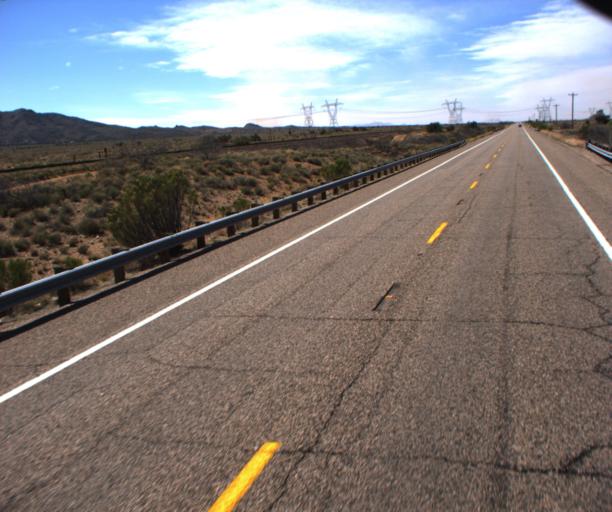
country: US
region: Arizona
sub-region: Mohave County
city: New Kingman-Butler
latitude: 35.3909
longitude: -113.7427
